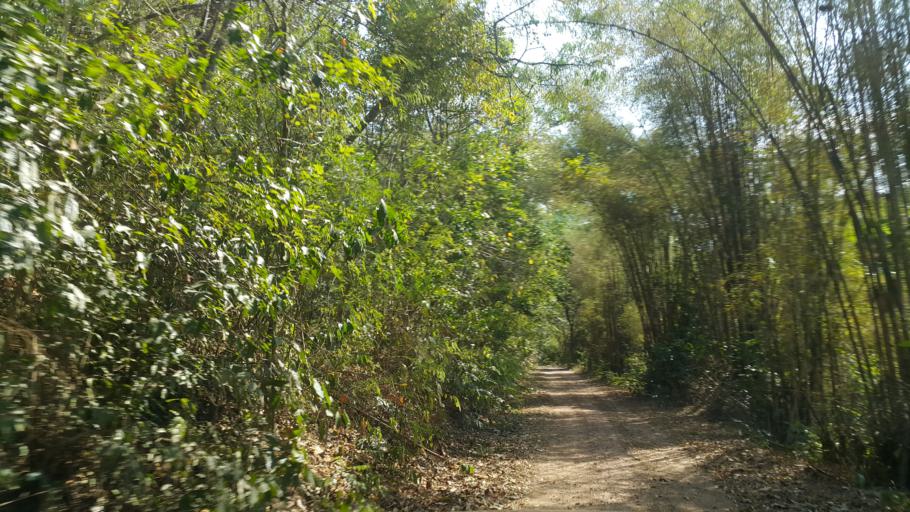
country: TH
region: Sukhothai
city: Thung Saliam
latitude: 17.3405
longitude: 99.5849
